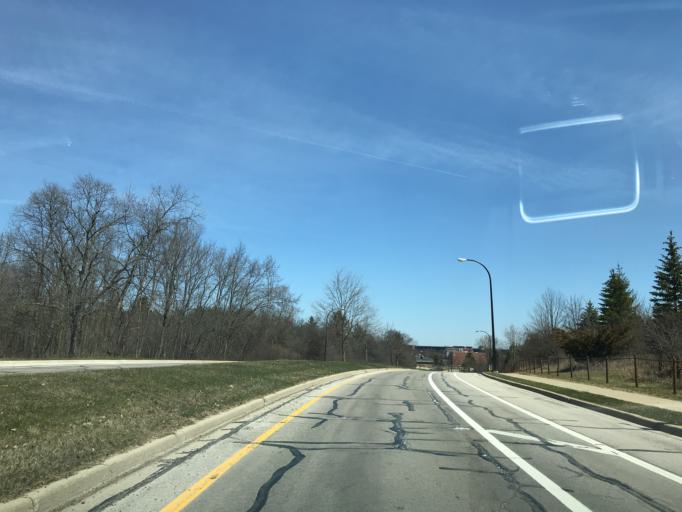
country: US
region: Michigan
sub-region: Washtenaw County
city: Ann Arbor
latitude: 42.2581
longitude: -83.7601
